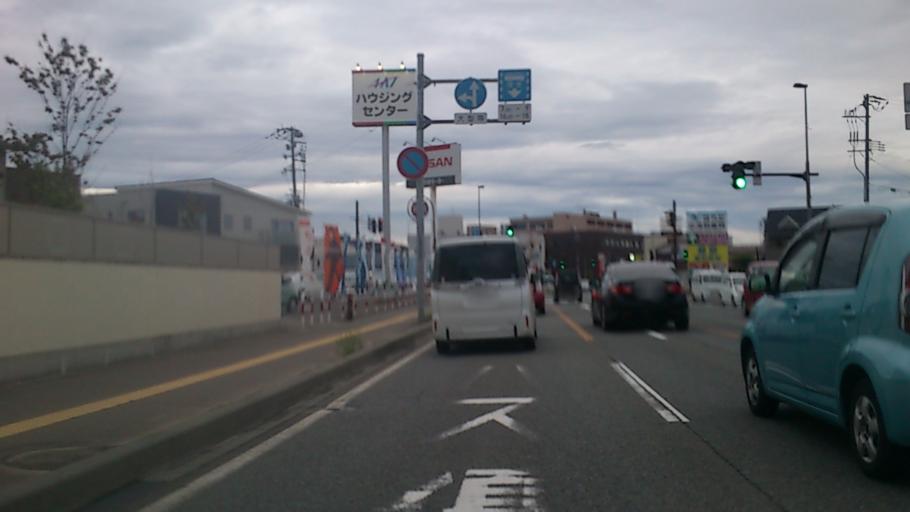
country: JP
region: Akita
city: Akita Shi
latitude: 39.7256
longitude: 140.1074
